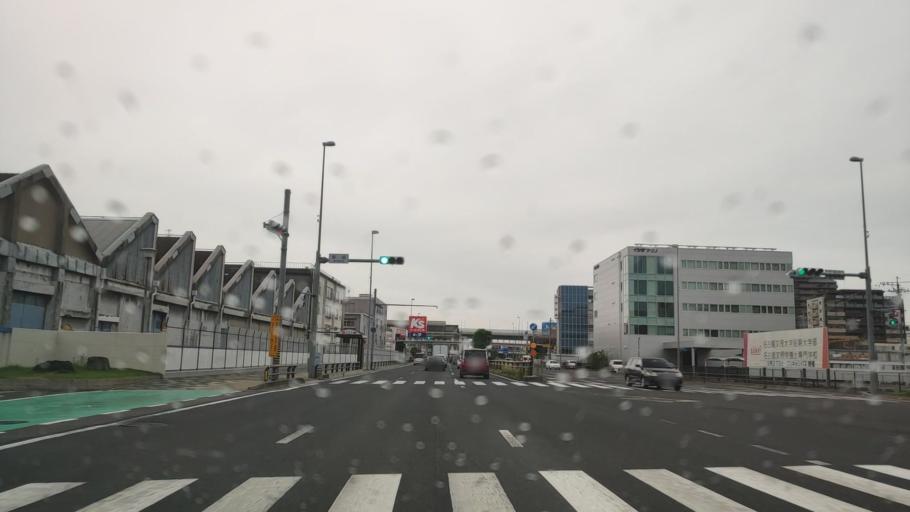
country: JP
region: Aichi
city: Nagoya-shi
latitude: 35.1990
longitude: 136.8815
